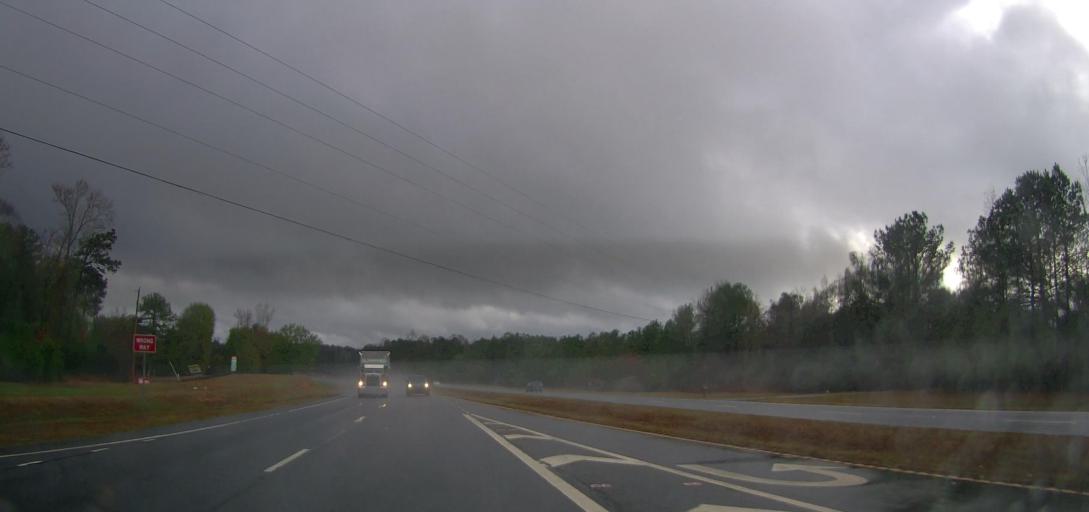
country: US
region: Georgia
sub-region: Clarke County
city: Country Club Estates
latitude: 34.0310
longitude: -83.4018
